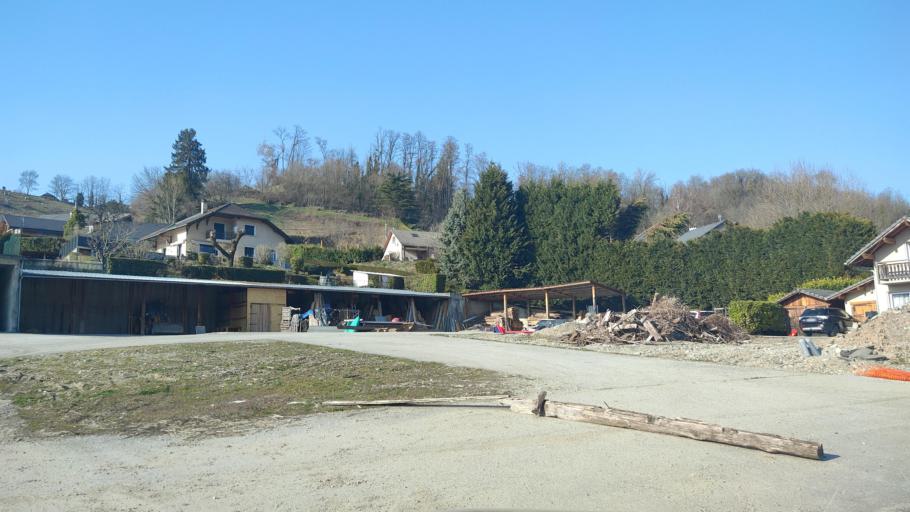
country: FR
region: Rhone-Alpes
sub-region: Departement de la Savoie
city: Coise-Saint-Jean-Pied-Gauthier
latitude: 45.5275
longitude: 6.1449
